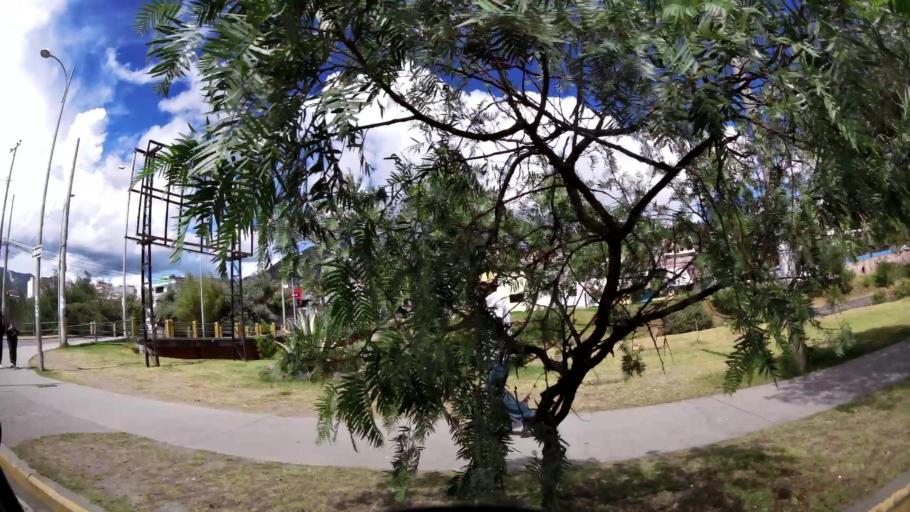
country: EC
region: Canar
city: Azogues
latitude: -2.7447
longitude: -78.8501
